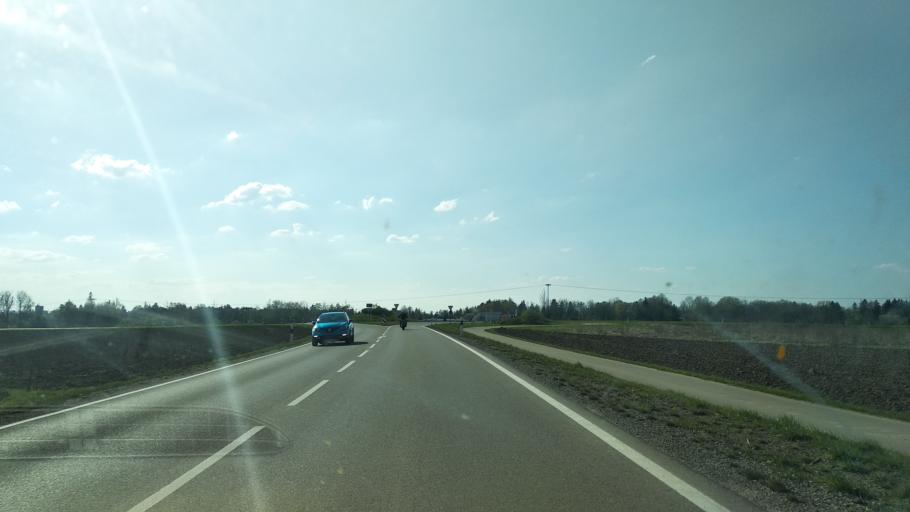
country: DE
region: Bavaria
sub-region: Swabia
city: Benningen
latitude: 47.9739
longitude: 10.2123
